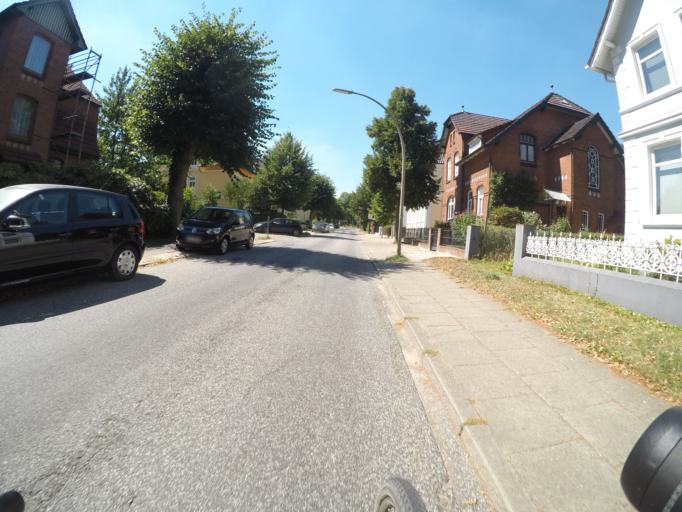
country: DE
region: Hamburg
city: Bergedorf
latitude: 53.4957
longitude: 10.2002
